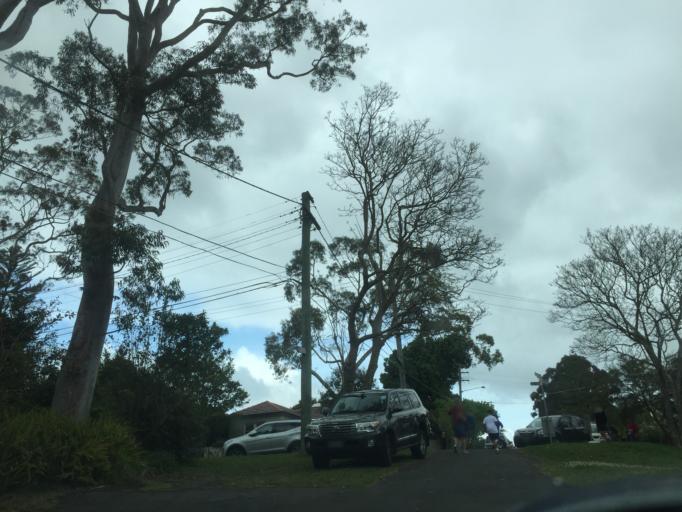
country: AU
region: New South Wales
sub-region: Willoughby
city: Lane Cove North
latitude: -33.8026
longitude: 151.1578
